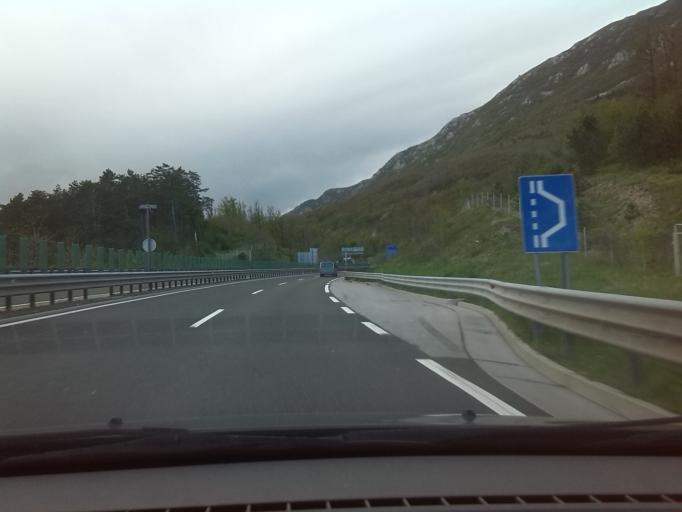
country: SI
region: Divaca
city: Divaca
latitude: 45.7587
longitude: 14.0454
